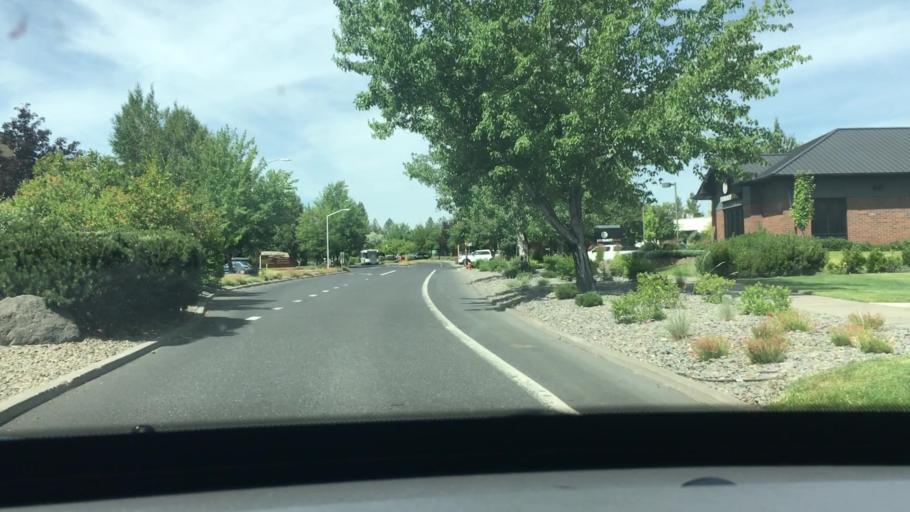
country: US
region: Oregon
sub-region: Deschutes County
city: Bend
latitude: 44.0443
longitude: -121.3242
